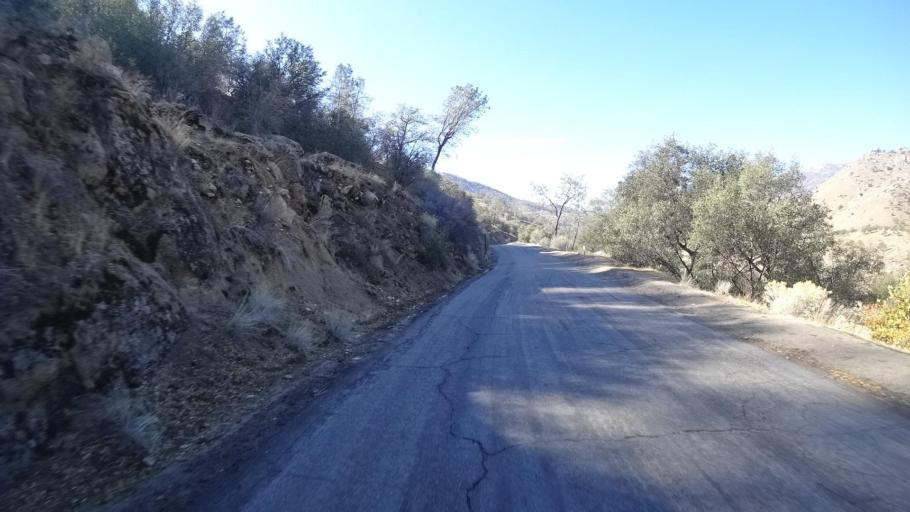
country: US
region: California
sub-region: Kern County
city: Bodfish
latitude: 35.5542
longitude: -118.5802
